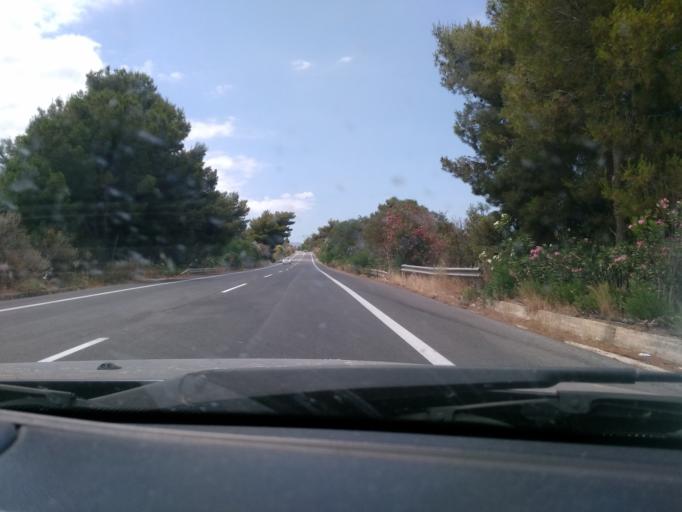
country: GR
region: Crete
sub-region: Nomos Chanias
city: Georgioupolis
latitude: 35.3645
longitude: 24.2365
